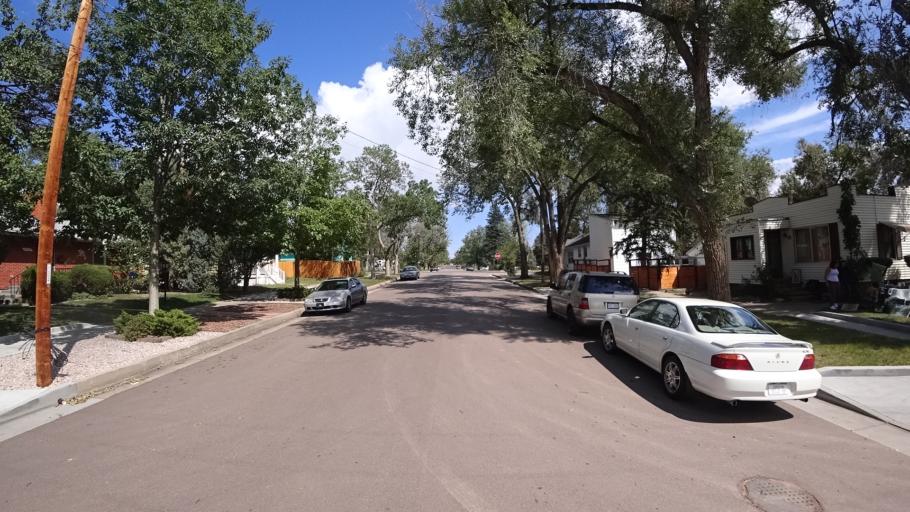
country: US
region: Colorado
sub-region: El Paso County
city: Colorado Springs
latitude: 38.8473
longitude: -104.8038
